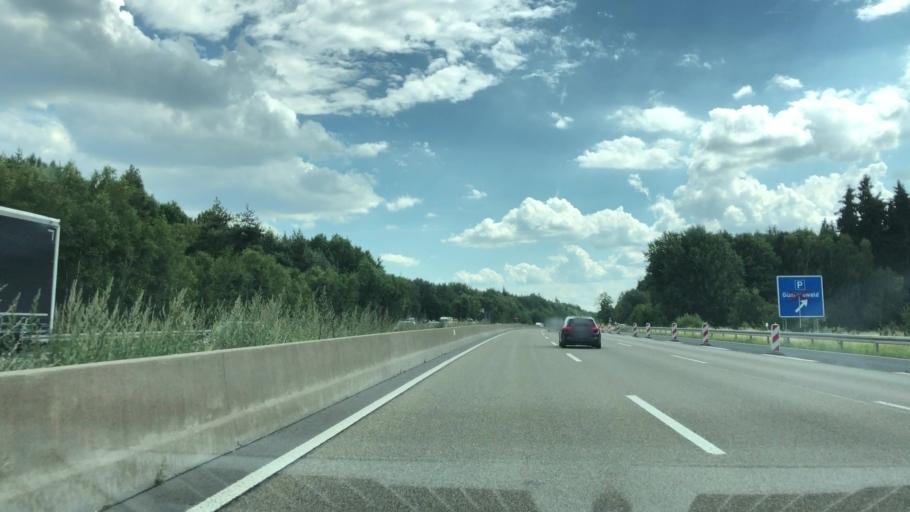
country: DE
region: Hesse
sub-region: Regierungsbezirk Kassel
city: Burghaun
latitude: 50.6871
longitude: 9.6833
